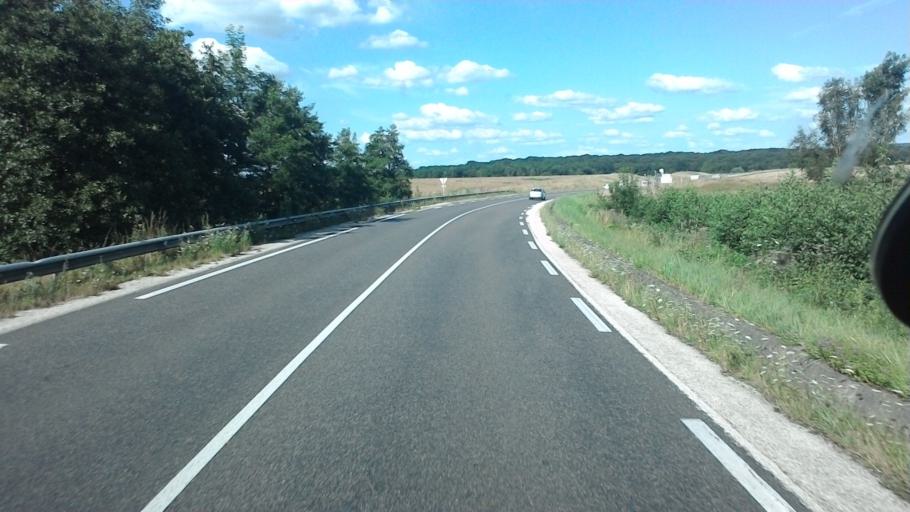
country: FR
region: Franche-Comte
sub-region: Departement de la Haute-Saone
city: Rioz
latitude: 47.4956
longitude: 5.9371
